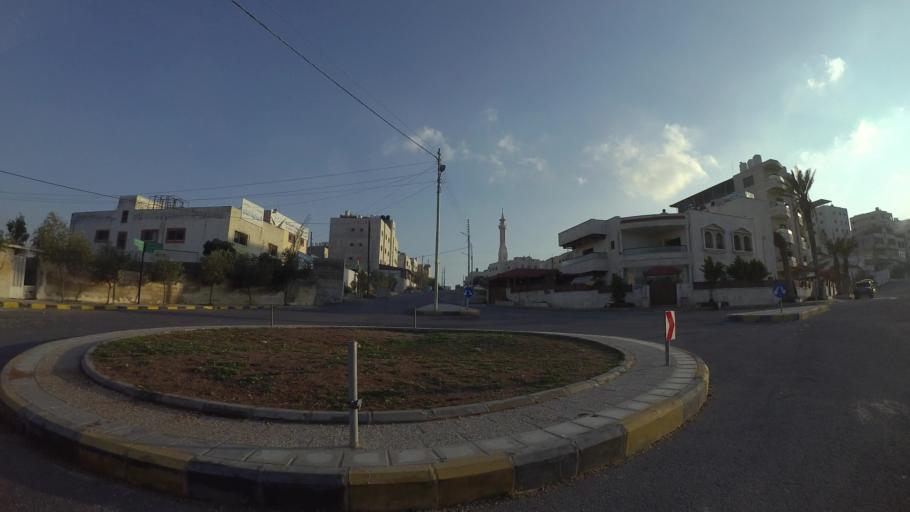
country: JO
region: Amman
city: Amman
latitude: 31.9869
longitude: 35.9731
